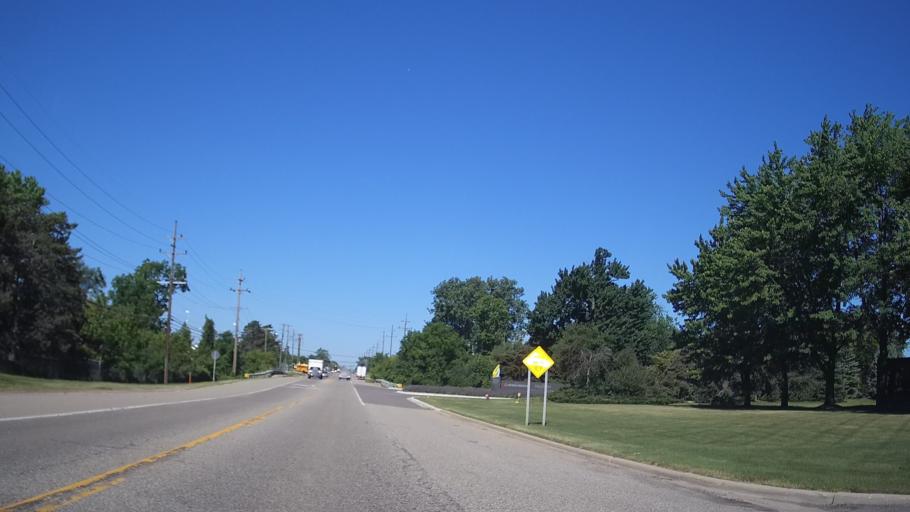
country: US
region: Michigan
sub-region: Macomb County
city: Sterling Heights
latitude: 42.5946
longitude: -83.0420
